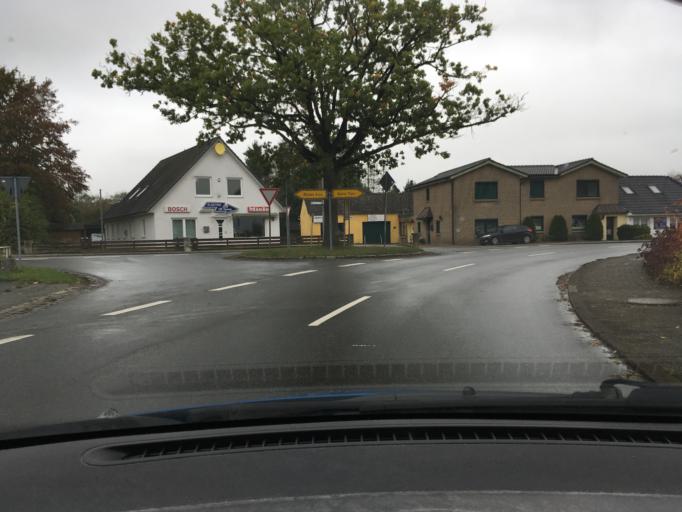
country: DE
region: Schleswig-Holstein
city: Bosau
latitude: 54.0890
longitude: 10.4754
